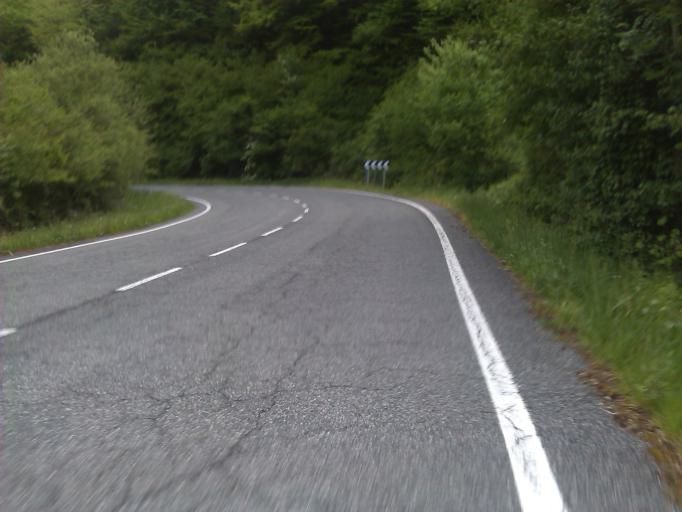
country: ES
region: Navarre
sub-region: Provincia de Navarra
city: Lekunberri
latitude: 43.0268
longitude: -1.9080
